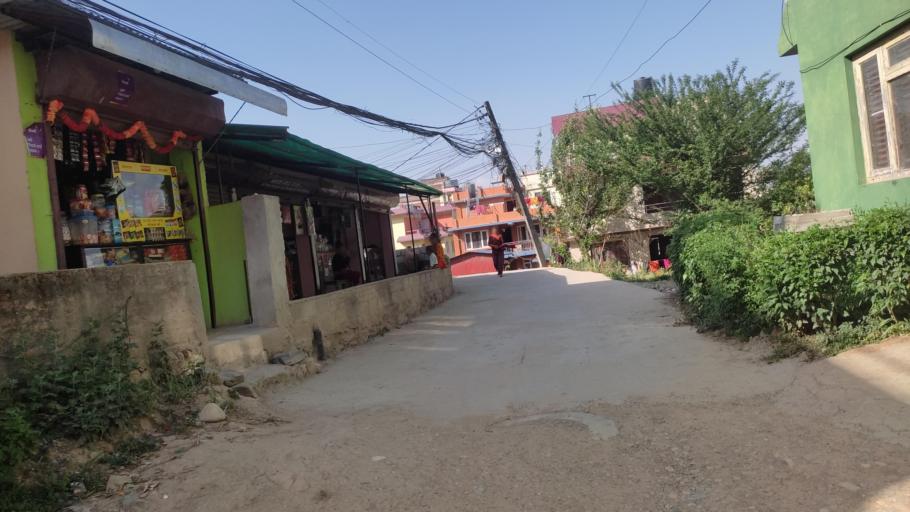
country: NP
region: Central Region
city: Kirtipur
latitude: 27.6657
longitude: 85.2662
